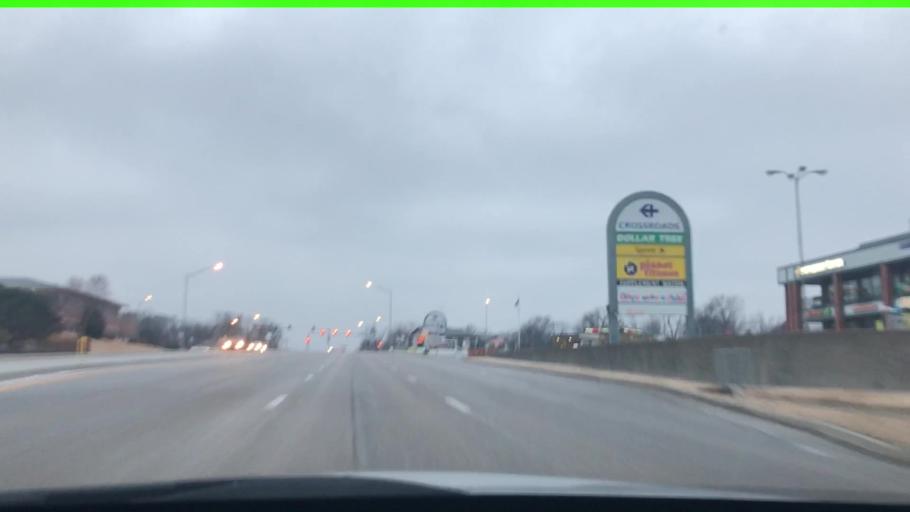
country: US
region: Missouri
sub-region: Boone County
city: Columbia
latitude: 38.9561
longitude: -92.3708
